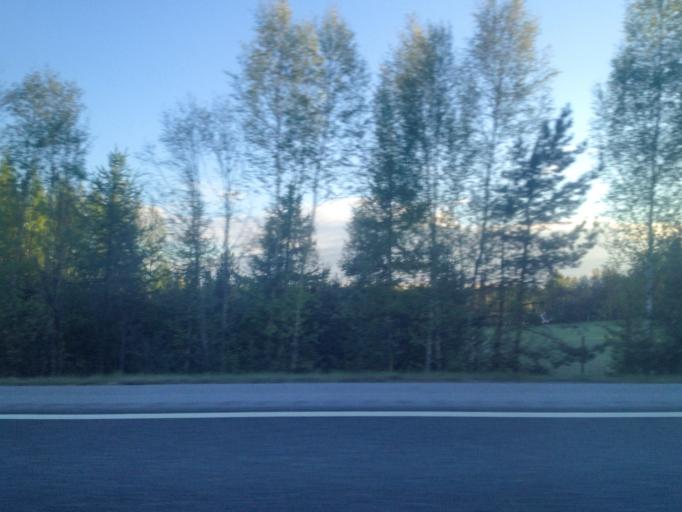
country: FI
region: Haeme
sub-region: Haemeenlinna
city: Janakkala
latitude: 60.8915
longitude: 24.5621
